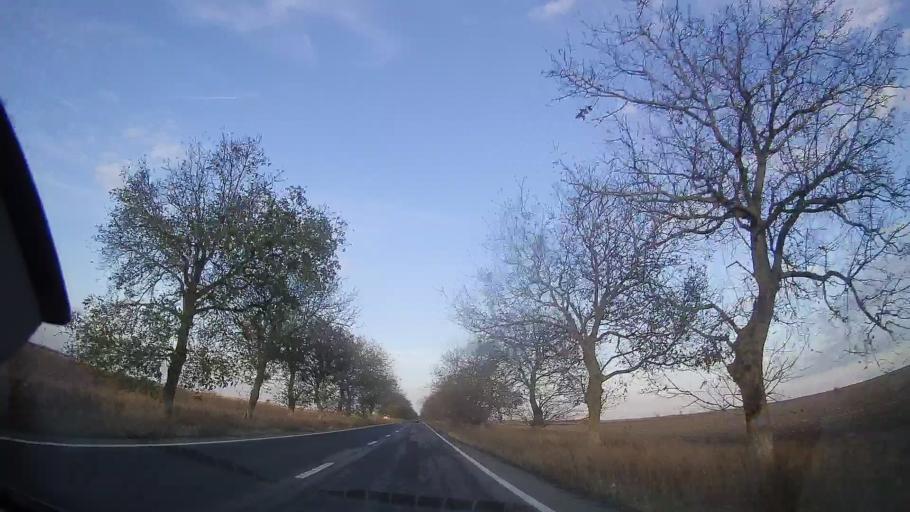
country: RO
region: Constanta
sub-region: Comuna Chirnogeni
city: Chirnogeni
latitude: 43.8678
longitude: 28.2693
